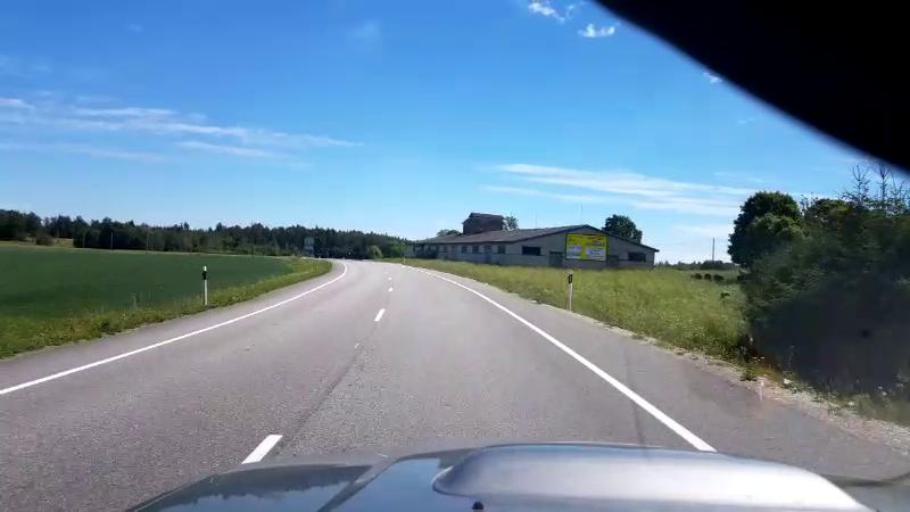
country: EE
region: Jaervamaa
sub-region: Jaerva-Jaani vald
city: Jarva-Jaani
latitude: 59.0023
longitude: 25.9329
